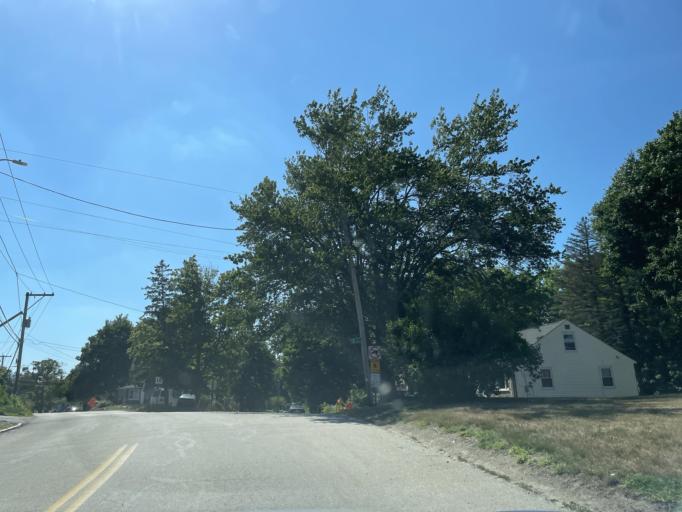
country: US
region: Massachusetts
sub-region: Worcester County
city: East Douglas
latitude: 42.0751
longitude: -71.7073
